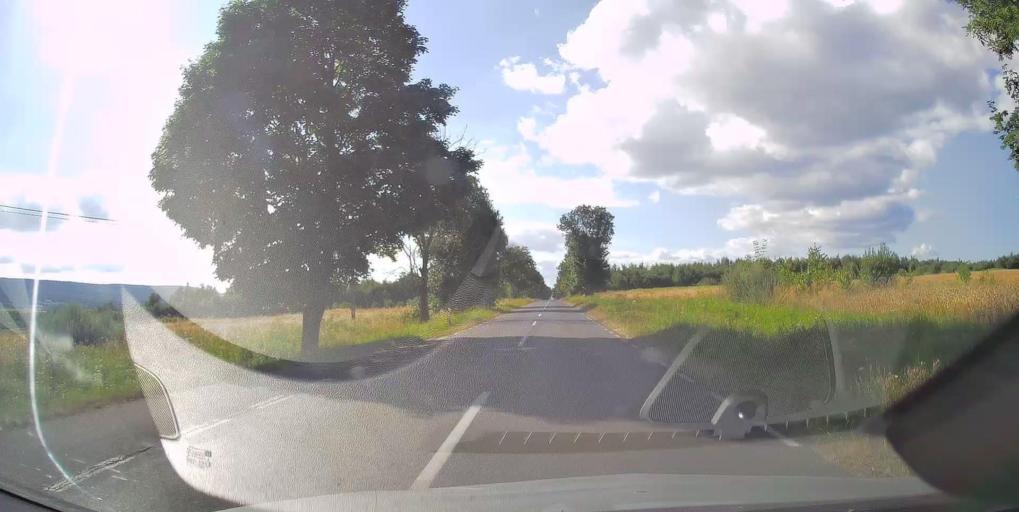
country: PL
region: Swietokrzyskie
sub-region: Powiat kielecki
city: Bodzentyn
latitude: 50.9575
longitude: 20.9116
